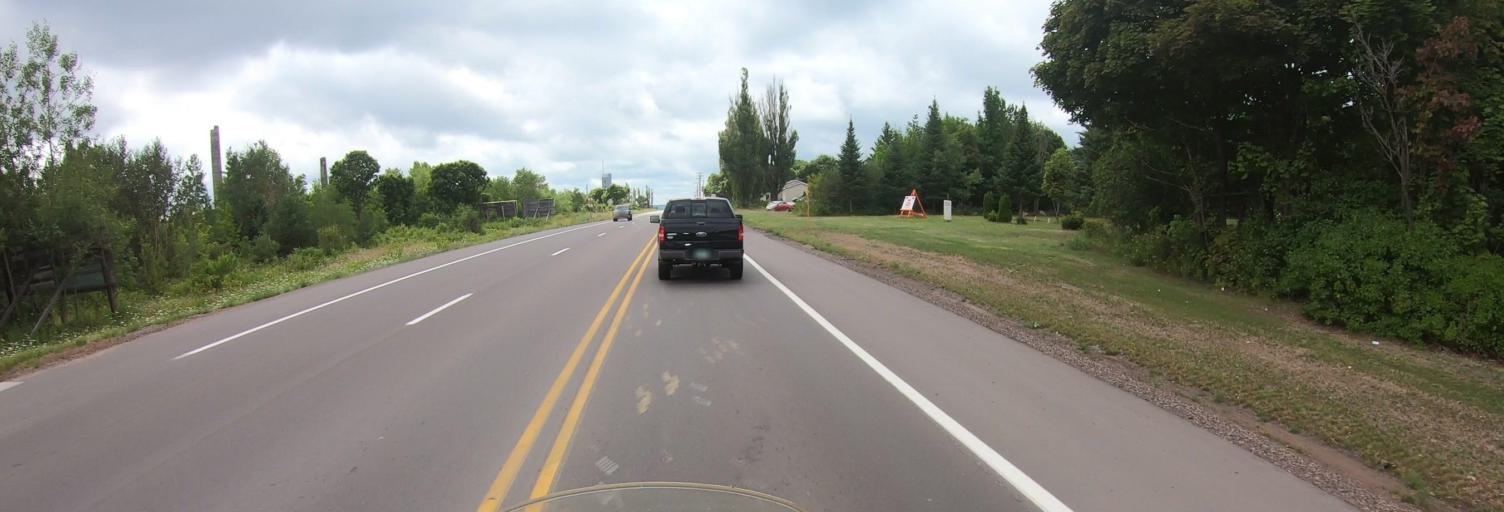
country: US
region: Michigan
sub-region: Houghton County
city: Hancock
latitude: 47.1426
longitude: -88.5703
